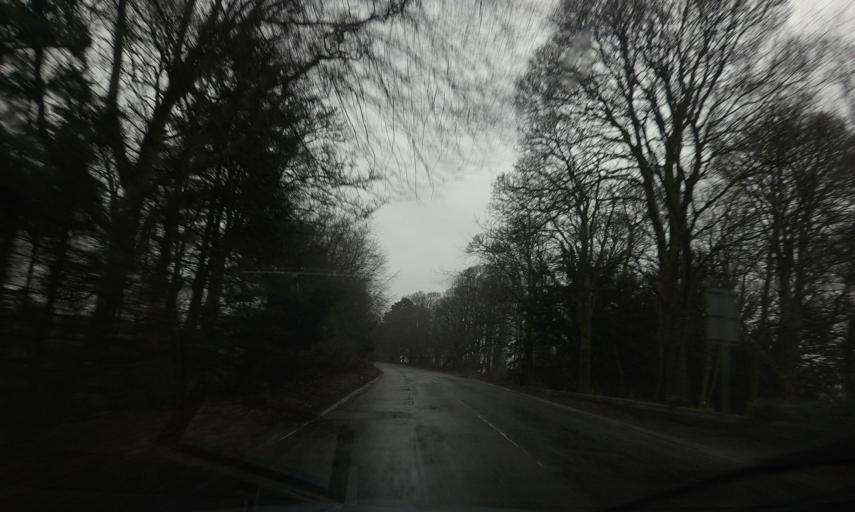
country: GB
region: Scotland
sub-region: East Dunbartonshire
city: Milngavie
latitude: 55.9436
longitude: -4.3491
